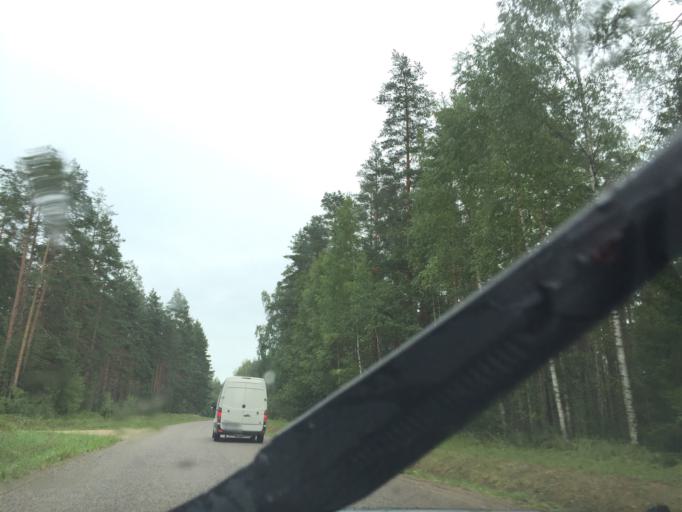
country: LV
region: Livani
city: Livani
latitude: 56.4512
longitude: 26.3295
